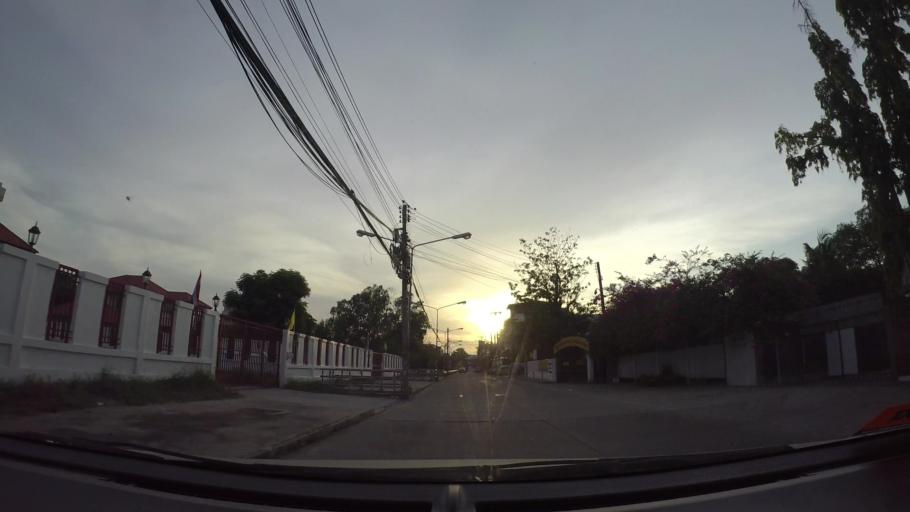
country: TH
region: Chon Buri
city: Chon Buri
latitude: 13.3565
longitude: 100.9802
